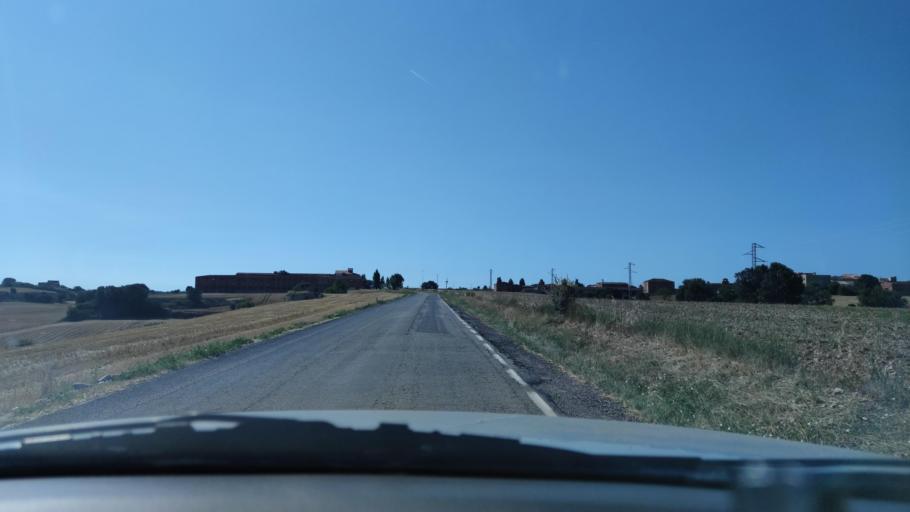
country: ES
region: Catalonia
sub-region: Provincia de Lleida
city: Sant Guim de Freixenet
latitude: 41.6623
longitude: 1.4211
